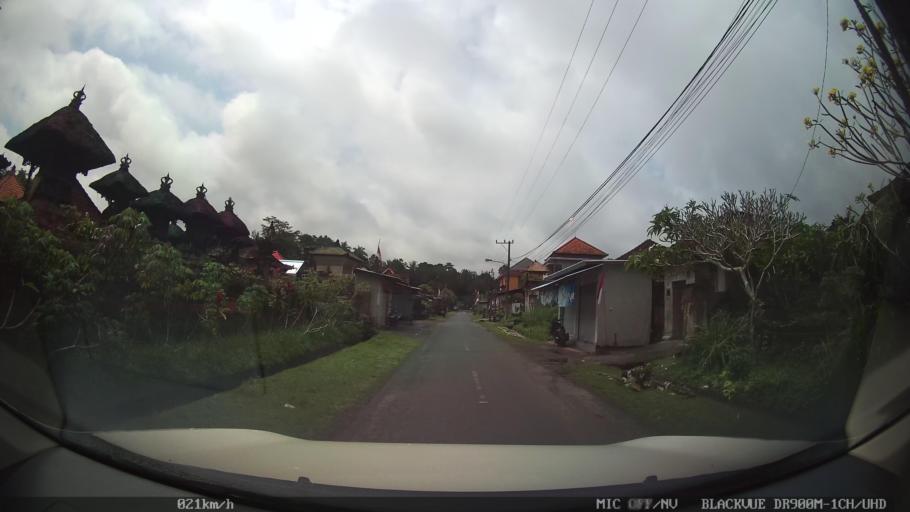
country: ID
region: Bali
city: Pegongan
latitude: -8.4837
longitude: 115.2271
